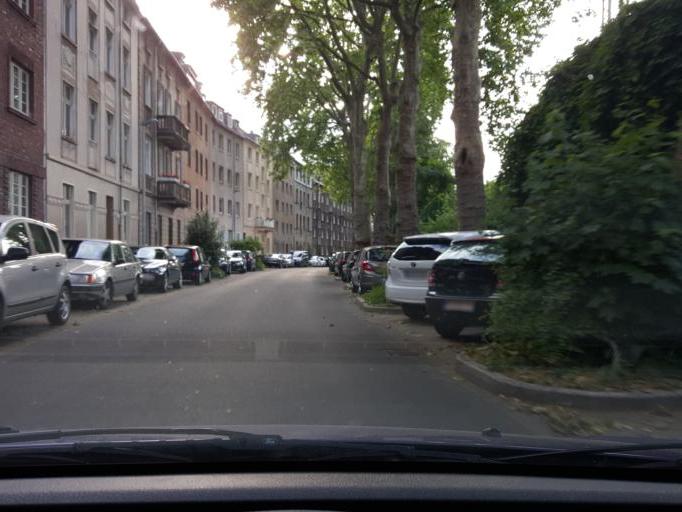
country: DE
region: North Rhine-Westphalia
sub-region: Regierungsbezirk Dusseldorf
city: Dusseldorf
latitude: 51.2074
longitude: 6.7700
